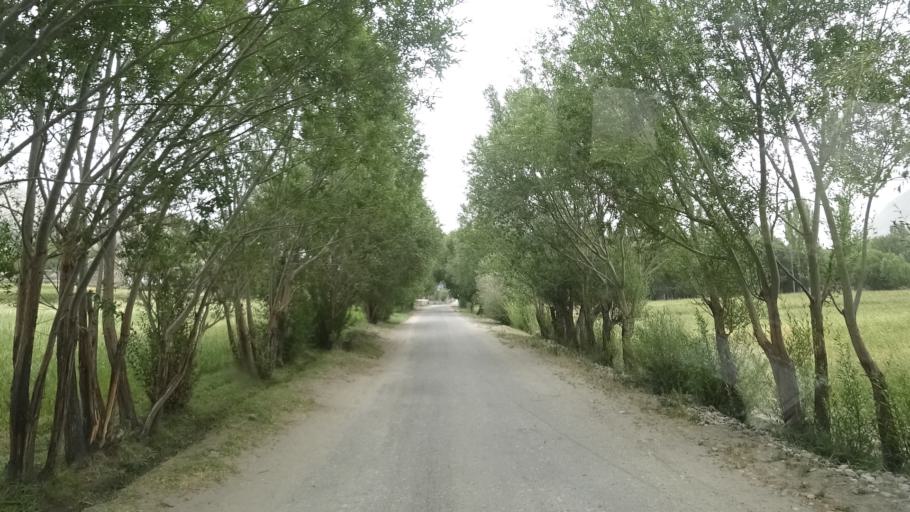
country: AF
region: Badakhshan
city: Khandud
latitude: 37.0314
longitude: 72.6268
